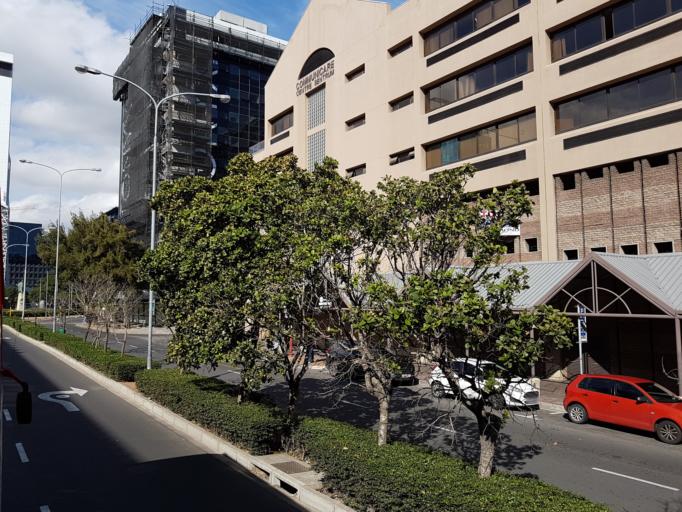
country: ZA
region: Western Cape
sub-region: City of Cape Town
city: Cape Town
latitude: -33.9167
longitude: 18.4269
